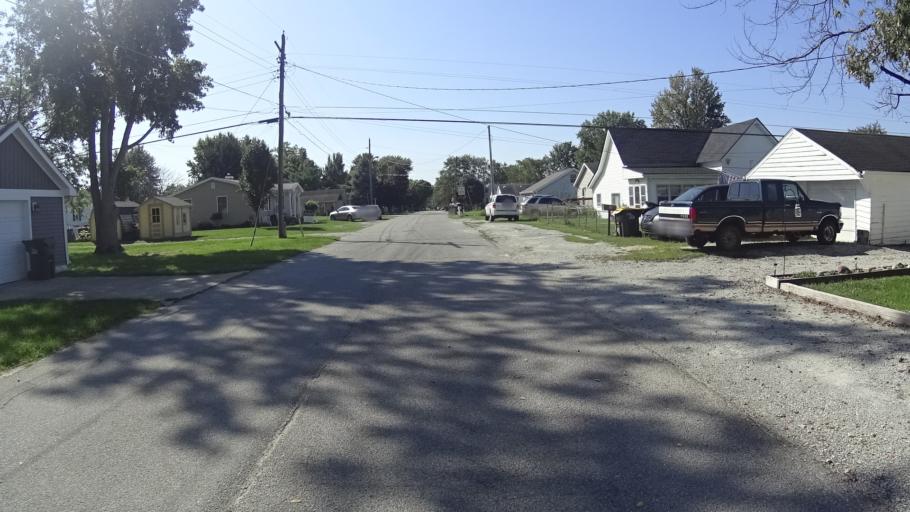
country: US
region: Indiana
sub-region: Madison County
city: Lapel
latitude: 40.0653
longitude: -85.8504
